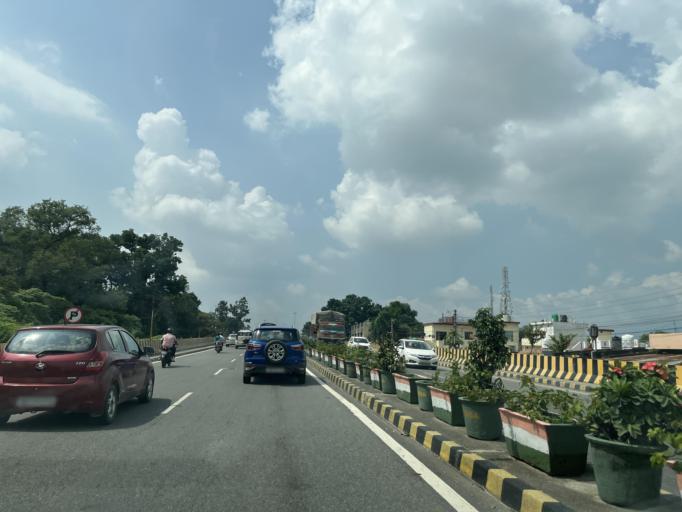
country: IN
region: Uttarakhand
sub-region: Dehradun
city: Raipur
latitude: 30.2741
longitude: 78.0768
